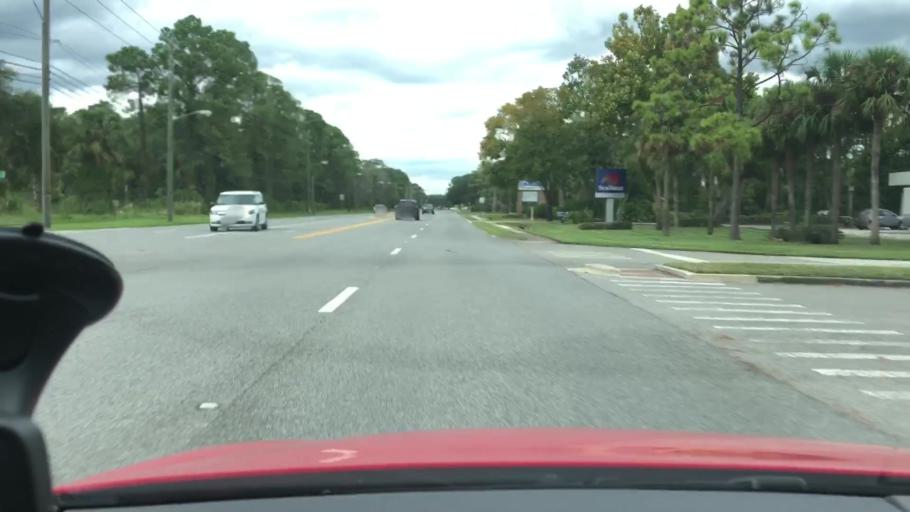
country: US
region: Florida
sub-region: Volusia County
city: Daytona Beach
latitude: 29.1971
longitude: -81.0689
